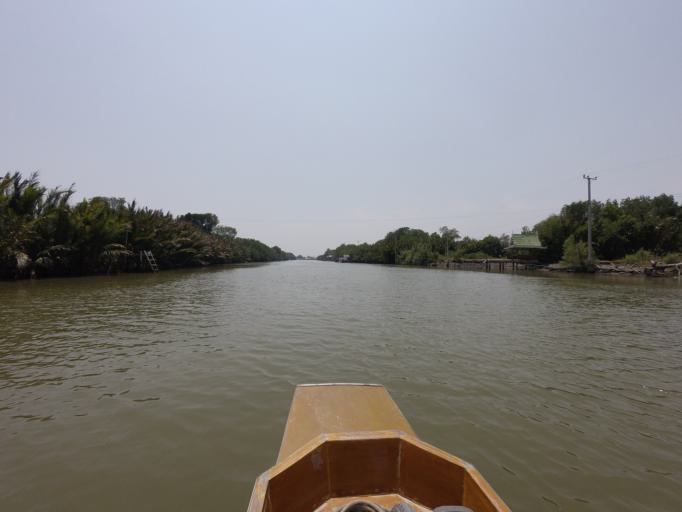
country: TH
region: Bangkok
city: Thung Khru
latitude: 13.5422
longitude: 100.4563
